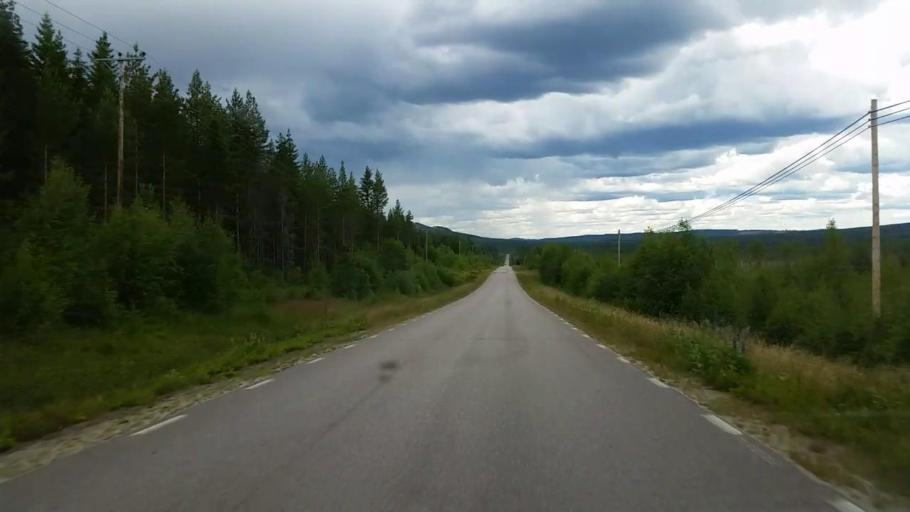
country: SE
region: Gaevleborg
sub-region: Ovanakers Kommun
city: Edsbyn
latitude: 61.4337
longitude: 15.8977
